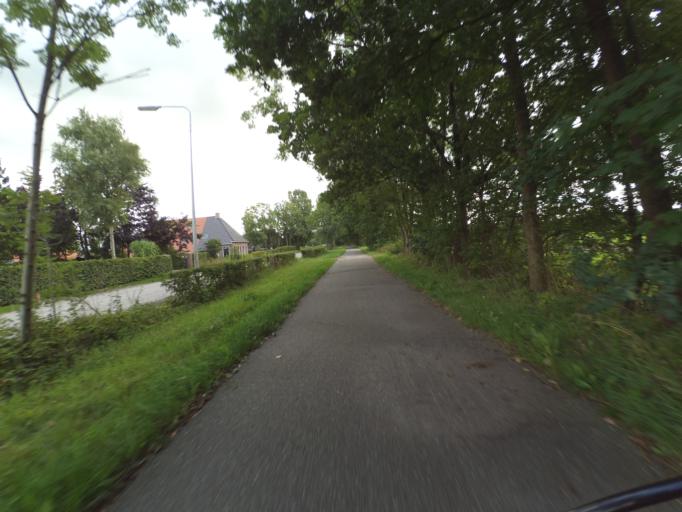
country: NL
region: Friesland
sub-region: Gemeente Tytsjerksteradiel
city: Burgum
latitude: 53.2059
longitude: 5.9753
